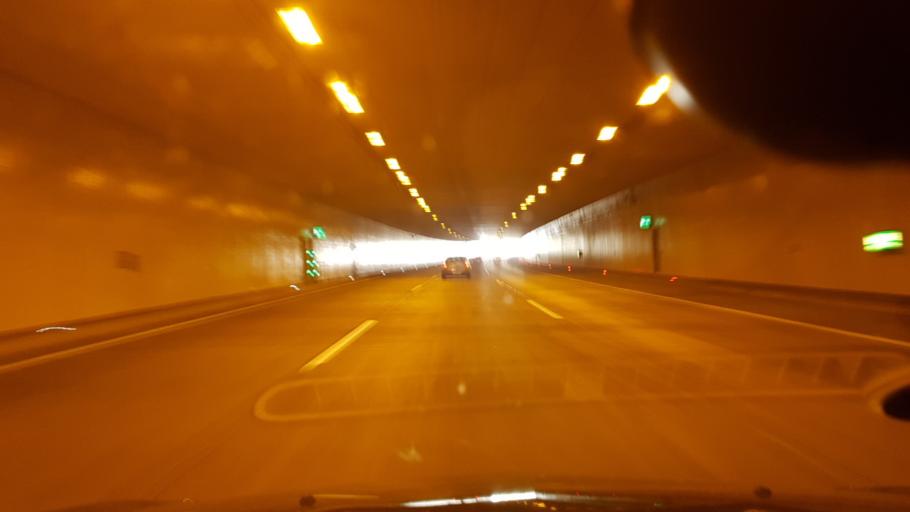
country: AT
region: Lower Austria
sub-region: Politischer Bezirk Mistelbach
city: Grossebersdorf
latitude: 48.3592
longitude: 16.4837
